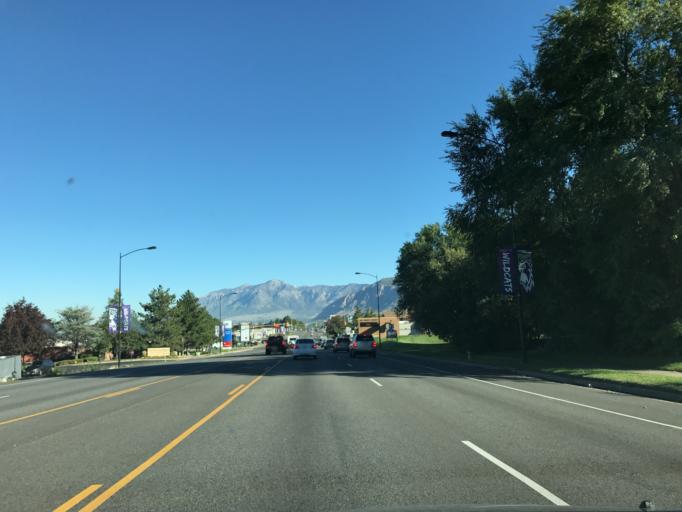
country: US
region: Utah
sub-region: Weber County
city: South Ogden
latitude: 41.1812
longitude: -111.9491
